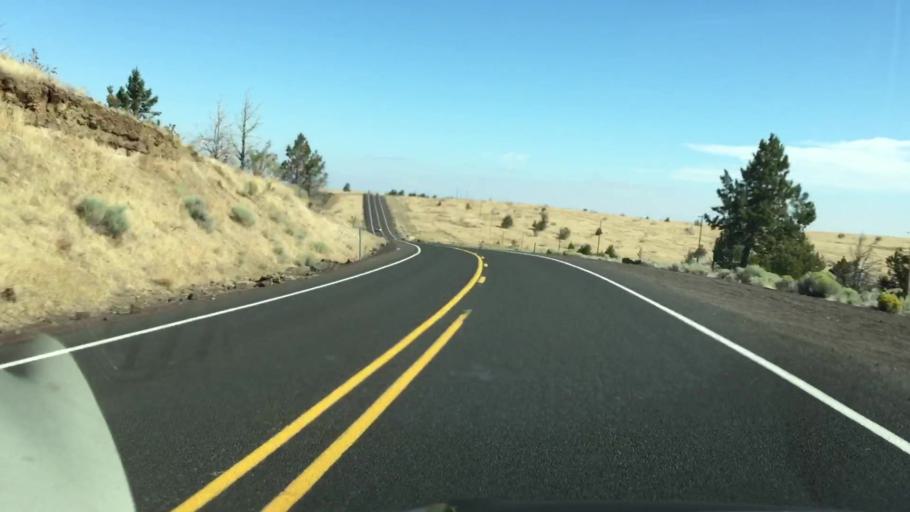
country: US
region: Oregon
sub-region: Jefferson County
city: Warm Springs
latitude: 45.0097
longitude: -120.9911
